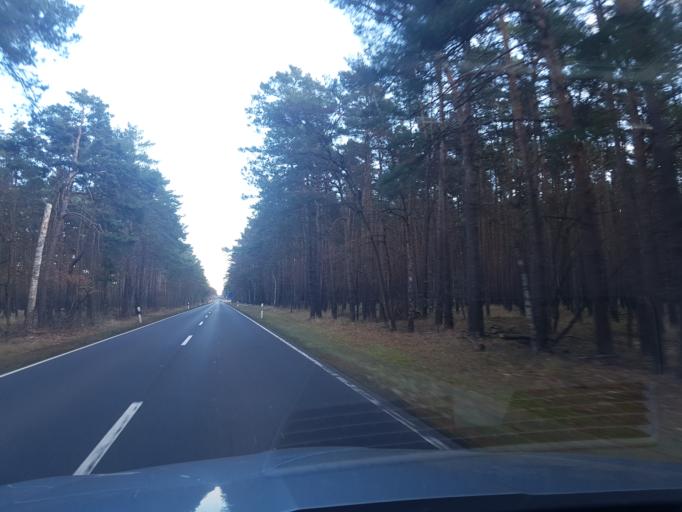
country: DE
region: Brandenburg
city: Kasel-Golzig
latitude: 52.0116
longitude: 13.6872
